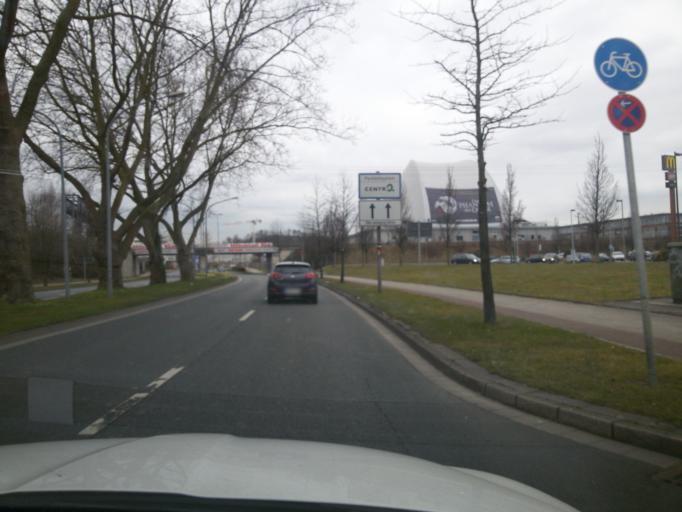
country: DE
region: North Rhine-Westphalia
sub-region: Regierungsbezirk Dusseldorf
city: Oberhausen
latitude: 51.4929
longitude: 6.8877
